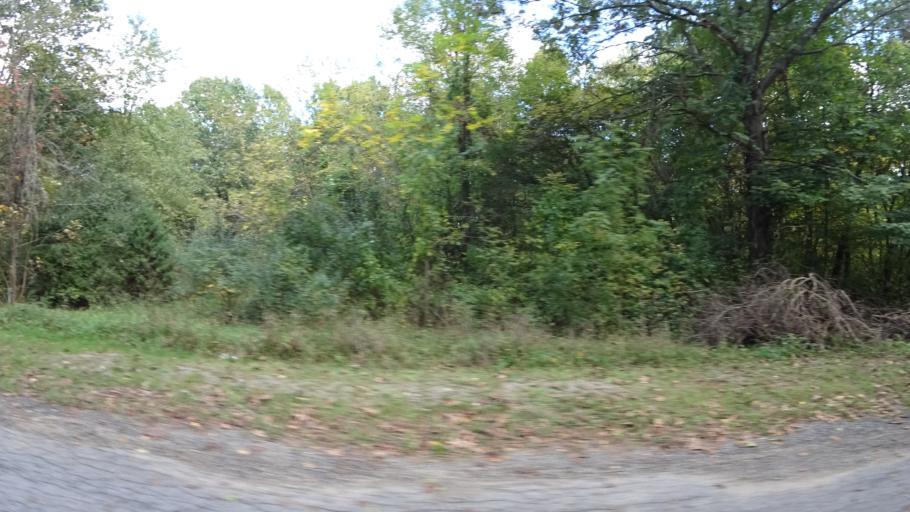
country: US
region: Michigan
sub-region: Saint Joseph County
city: Three Rivers
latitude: 41.9530
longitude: -85.5819
